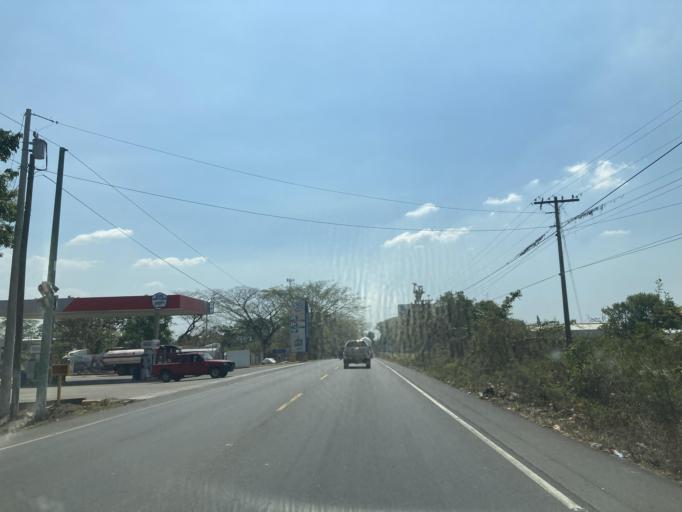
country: GT
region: Escuintla
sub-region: Municipio de Escuintla
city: Escuintla
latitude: 14.2309
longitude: -90.7373
